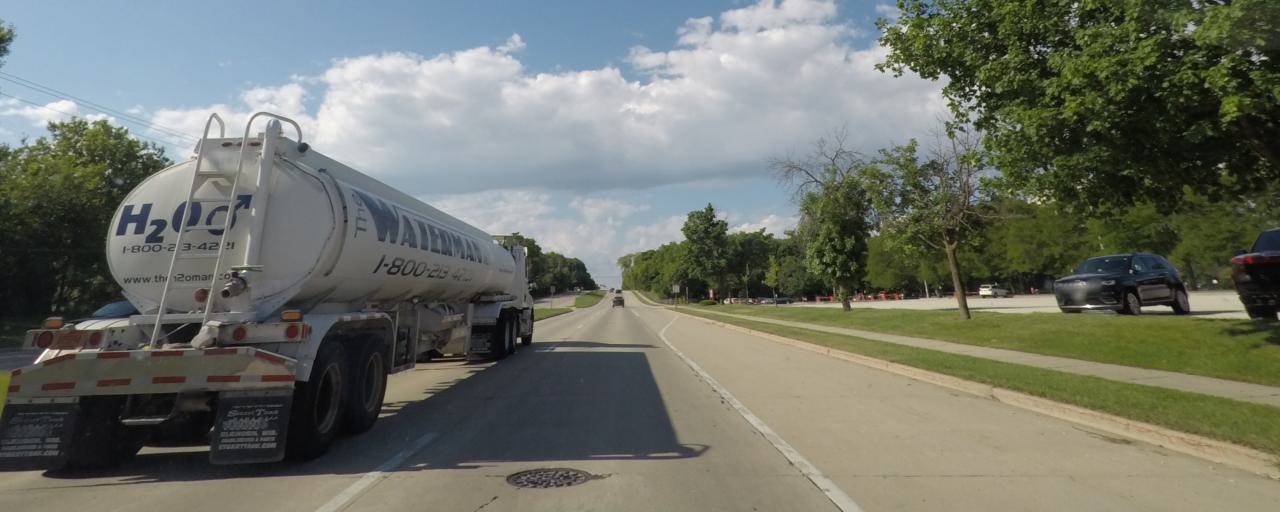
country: US
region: Wisconsin
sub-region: Milwaukee County
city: Greendale
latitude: 42.9310
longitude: -88.0087
